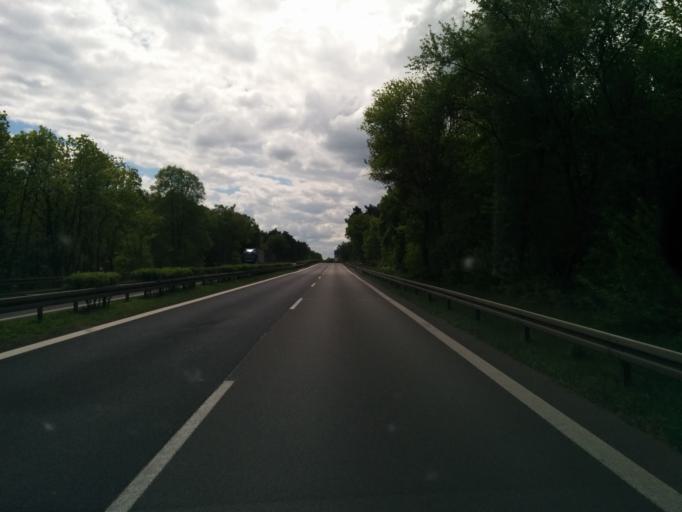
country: DE
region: Brandenburg
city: Werder
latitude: 52.4474
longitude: 12.9335
